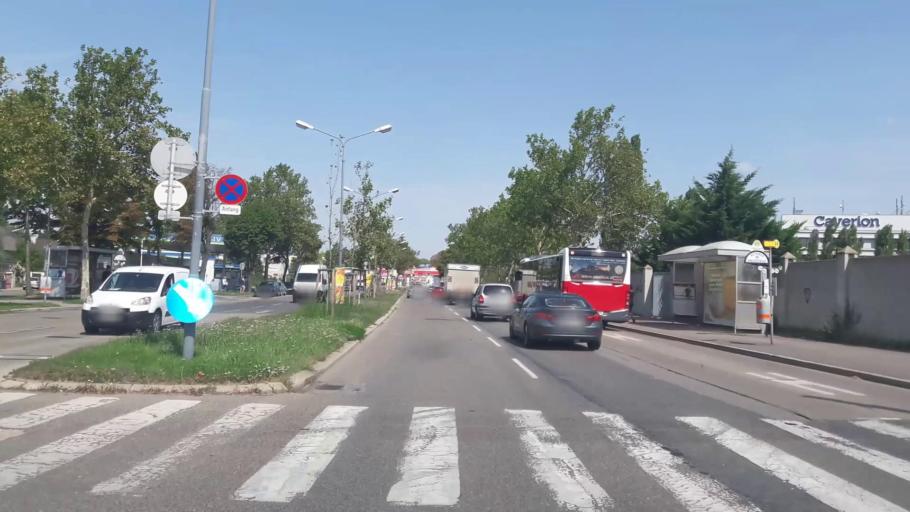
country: AT
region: Lower Austria
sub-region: Politischer Bezirk Modling
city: Vosendorf
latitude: 48.1456
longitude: 16.3615
